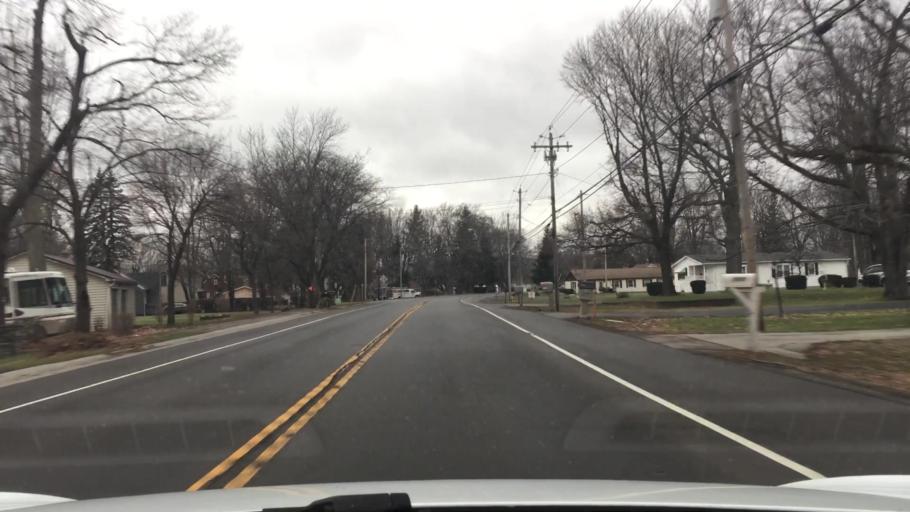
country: US
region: New York
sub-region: Erie County
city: Tonawanda
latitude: 43.0689
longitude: -78.9336
